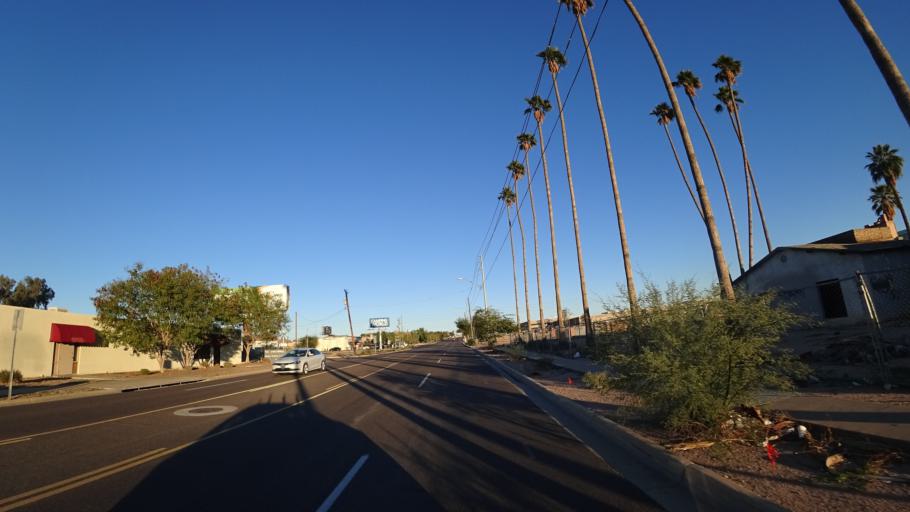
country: US
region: Arizona
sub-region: Maricopa County
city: Tempe Junction
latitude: 33.4511
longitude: -111.9808
